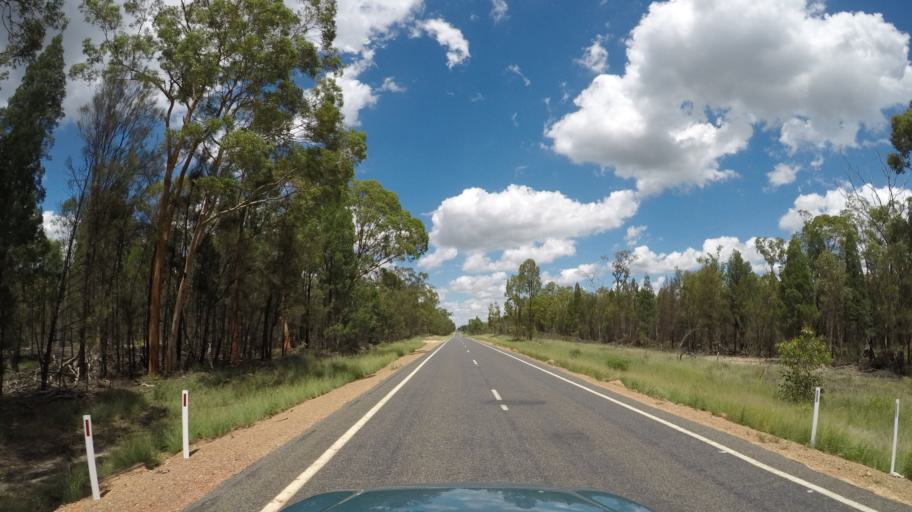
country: AU
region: Queensland
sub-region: Western Downs
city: Dalby
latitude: -27.9891
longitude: 150.9629
